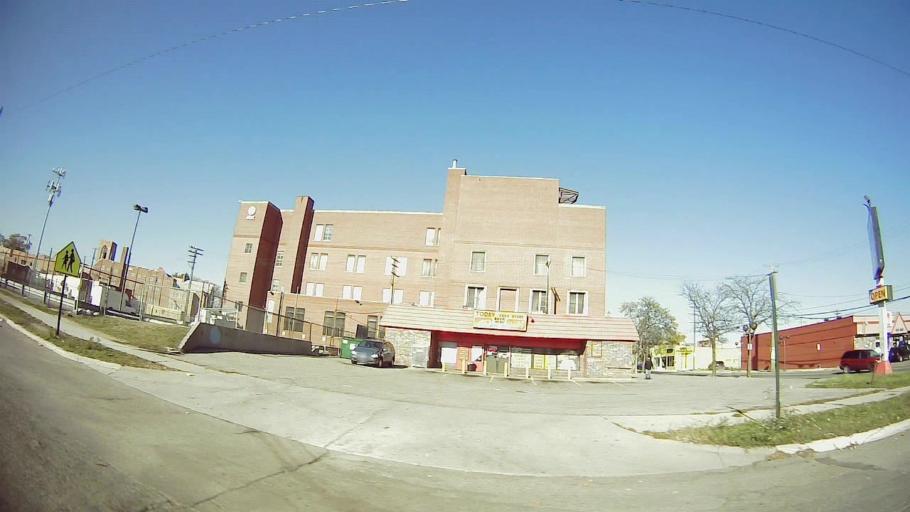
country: US
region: Michigan
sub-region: Wayne County
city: Redford
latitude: 42.4148
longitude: -83.2579
